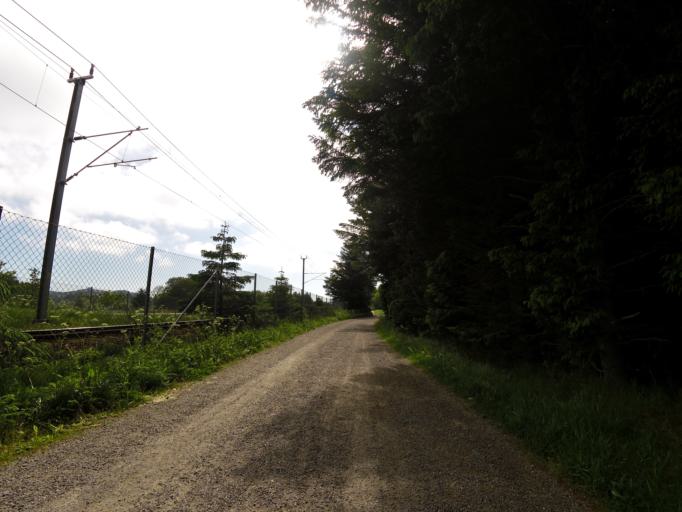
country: NO
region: Rogaland
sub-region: Ha
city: Vigrestad
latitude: 58.5248
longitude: 5.7906
